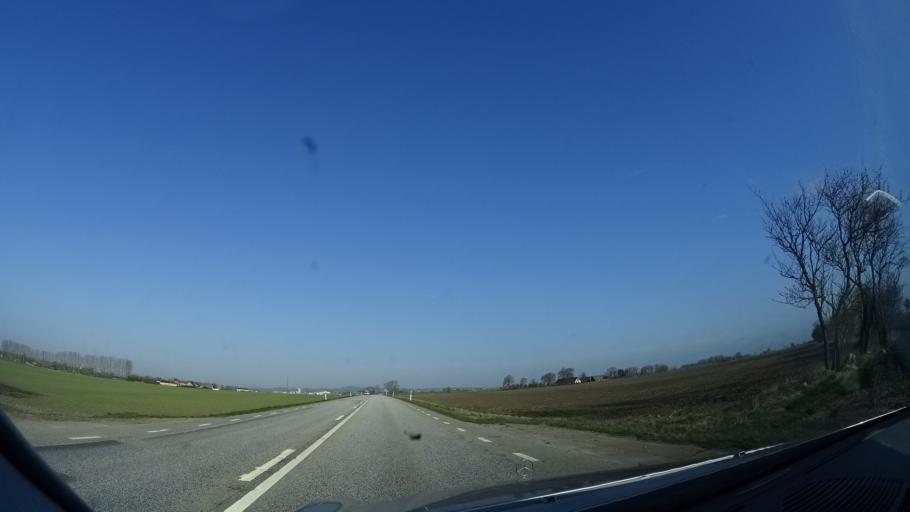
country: SE
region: Skane
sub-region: Svalovs Kommun
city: Teckomatorp
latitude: 55.8834
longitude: 13.0165
